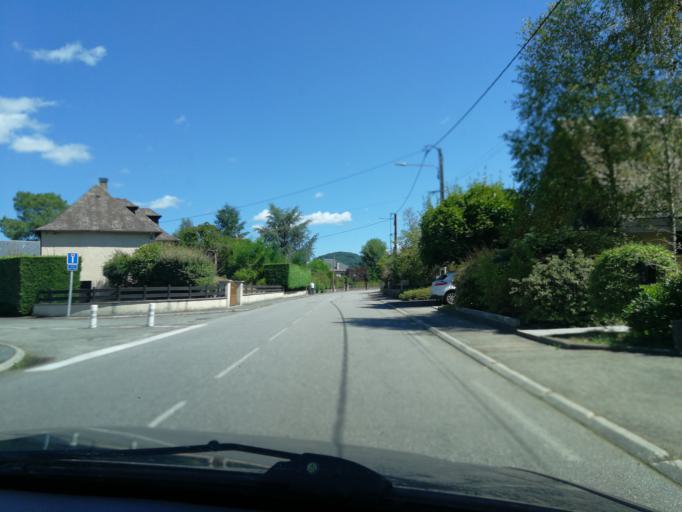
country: FR
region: Limousin
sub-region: Departement de la Correze
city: Argentat
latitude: 45.0901
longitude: 1.9294
